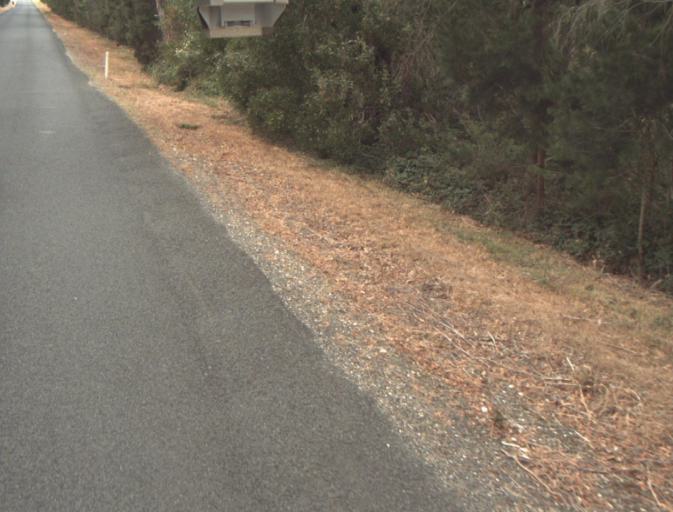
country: AU
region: Tasmania
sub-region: Launceston
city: Mayfield
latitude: -41.2166
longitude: 147.0519
